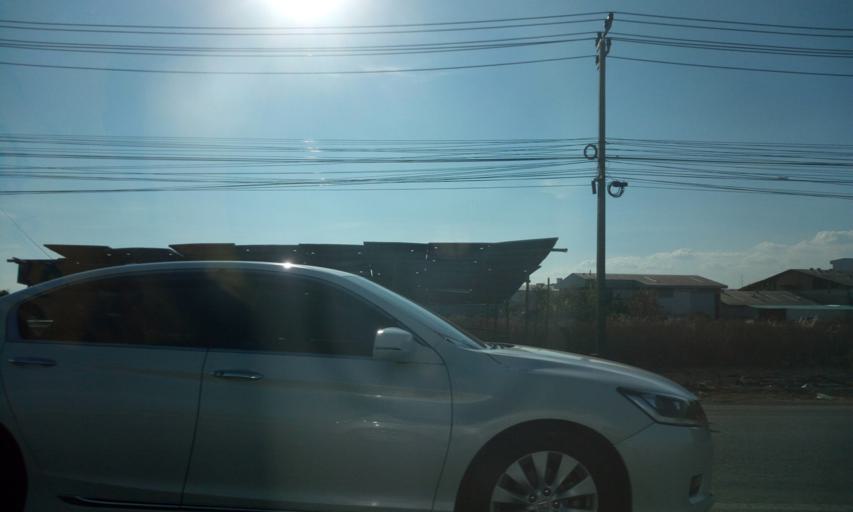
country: TH
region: Samut Prakan
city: Bang Bo District
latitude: 13.5901
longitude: 100.7607
